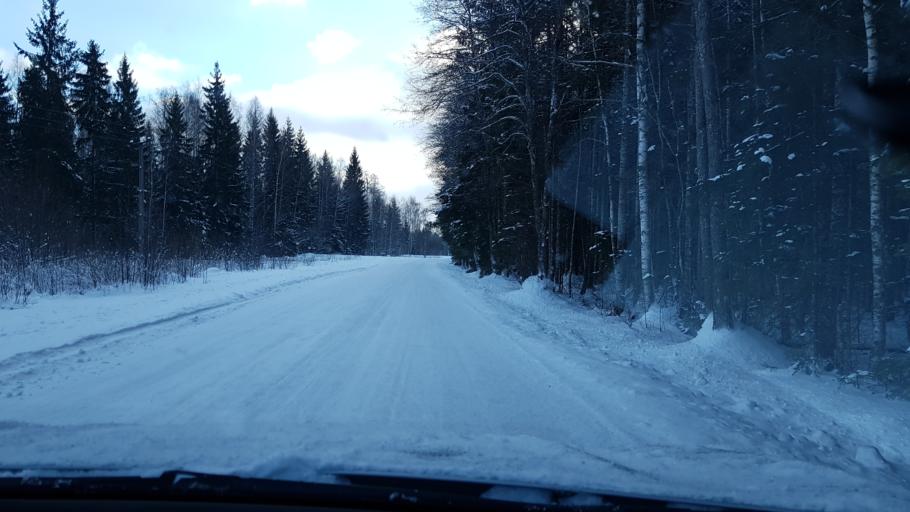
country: EE
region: Harju
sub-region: Nissi vald
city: Turba
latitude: 59.1568
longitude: 24.1440
